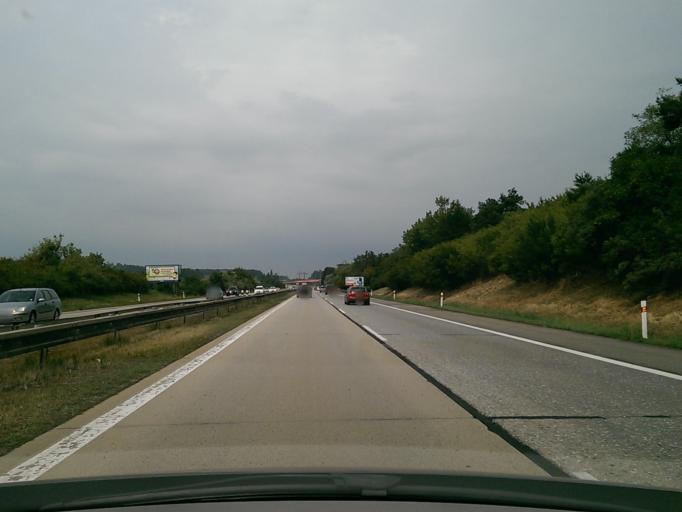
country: CZ
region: South Moravian
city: Ricany
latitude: 49.2492
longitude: 16.3571
